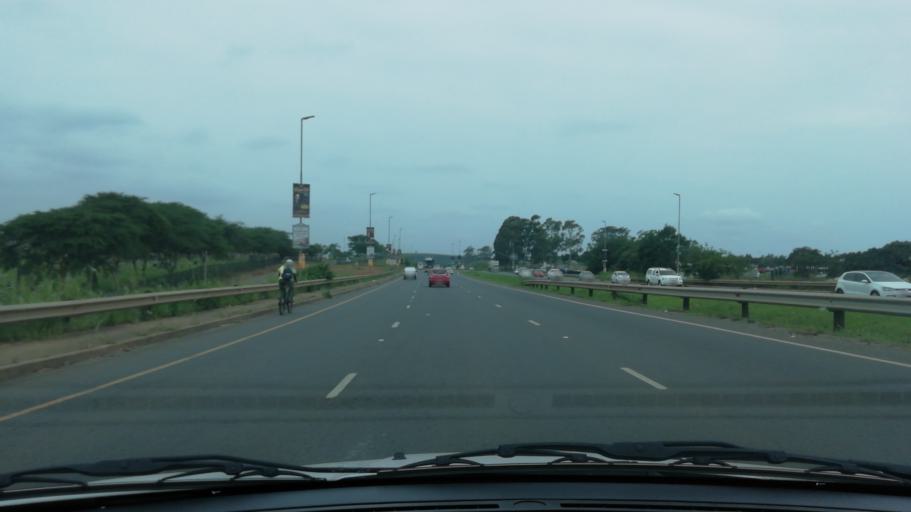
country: ZA
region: KwaZulu-Natal
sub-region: uThungulu District Municipality
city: Empangeni
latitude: -28.7669
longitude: 31.9120
